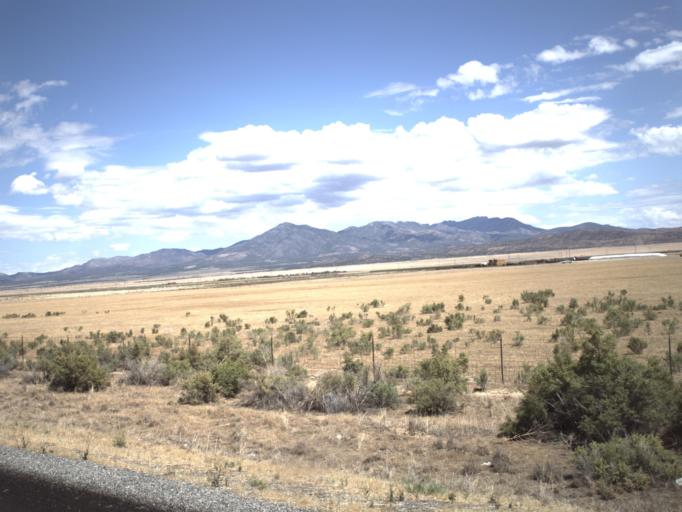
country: US
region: Utah
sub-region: Millard County
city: Fillmore
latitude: 39.1258
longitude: -112.3587
